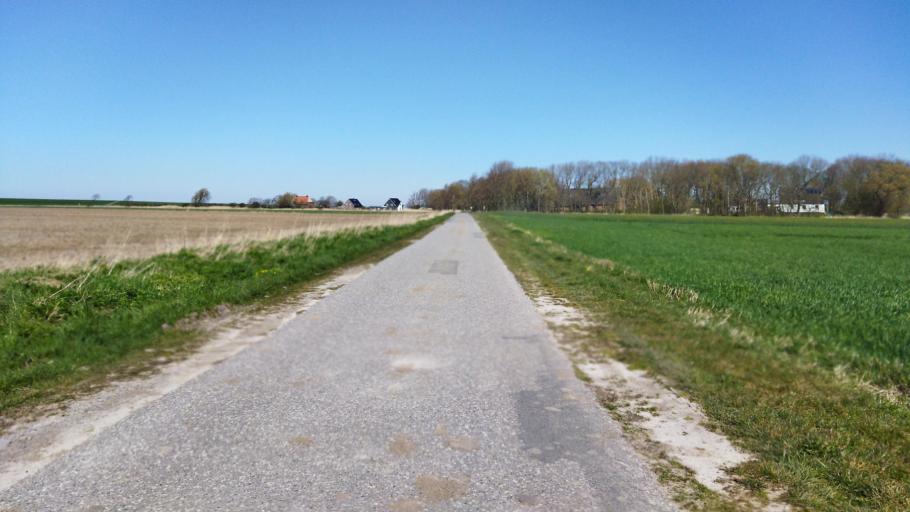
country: DE
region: Lower Saxony
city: Misselwarden
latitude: 53.6905
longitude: 8.4885
